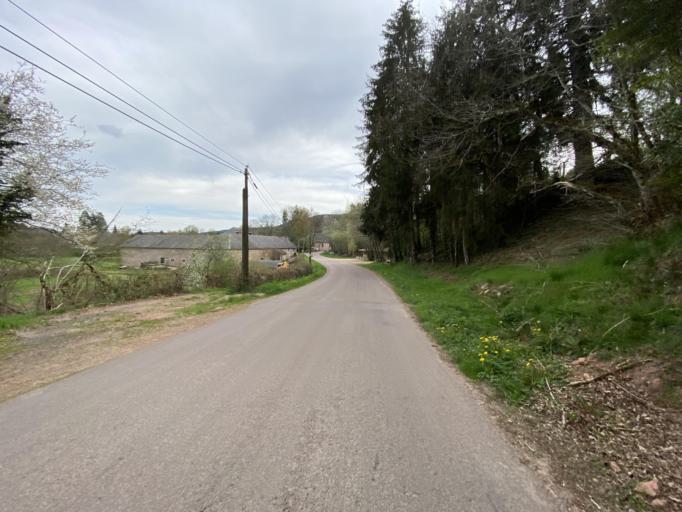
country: FR
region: Bourgogne
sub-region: Departement de la Cote-d'Or
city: Saulieu
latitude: 47.3198
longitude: 4.0944
